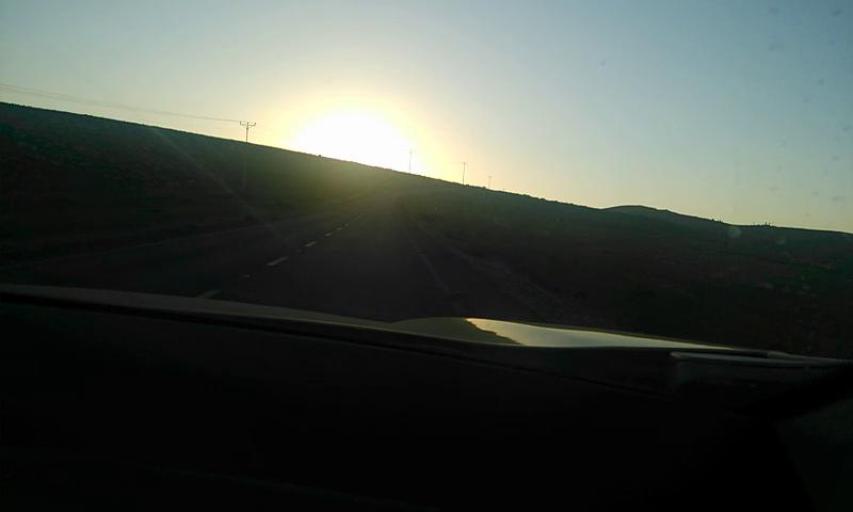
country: PS
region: West Bank
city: Rammun
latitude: 31.9182
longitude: 35.3338
